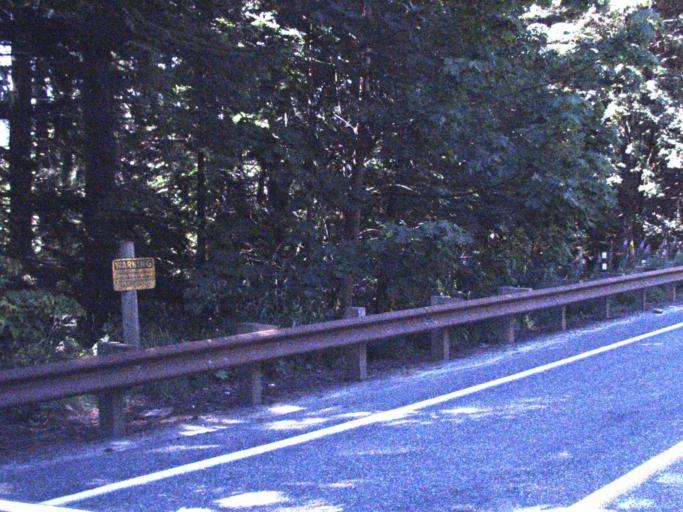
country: US
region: Washington
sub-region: King County
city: Enumclaw
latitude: 47.1683
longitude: -121.8109
